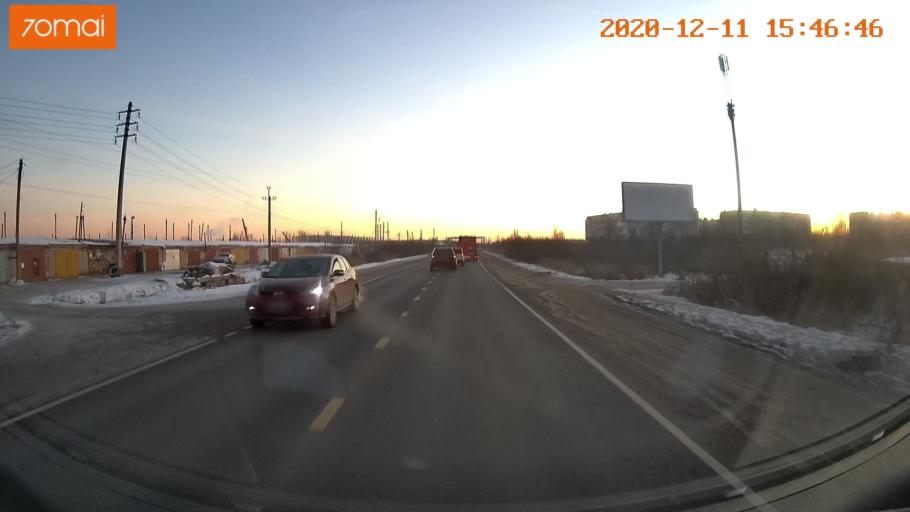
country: RU
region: Ivanovo
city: Novo-Talitsy
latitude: 57.0035
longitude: 40.8551
